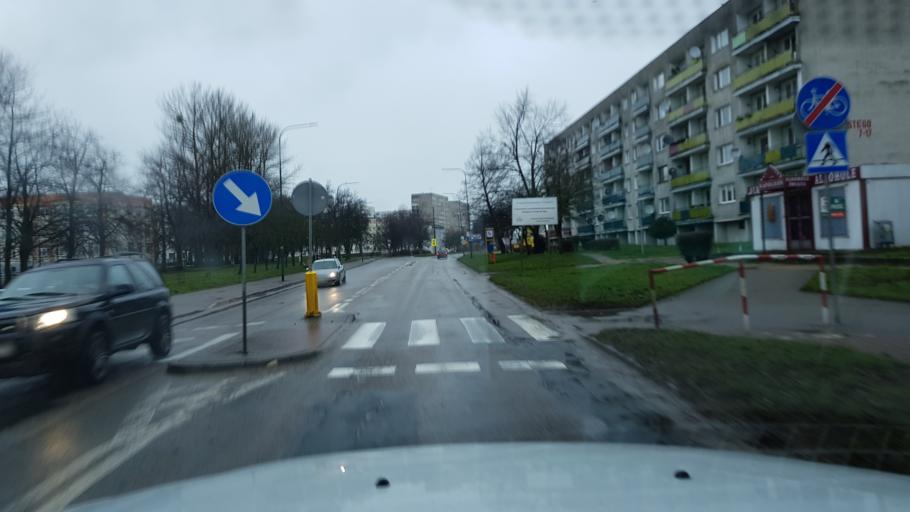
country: PL
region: West Pomeranian Voivodeship
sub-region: Powiat kolobrzeski
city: Kolobrzeg
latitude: 54.1728
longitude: 15.5890
